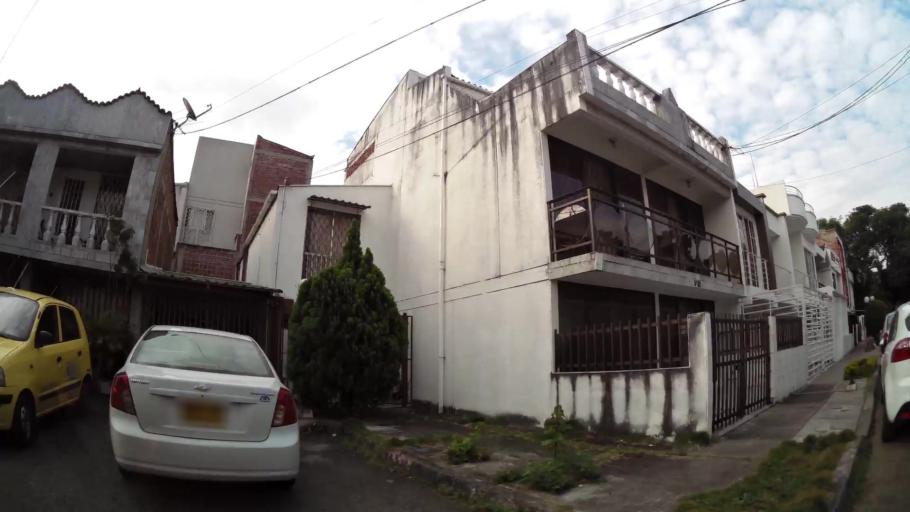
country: CO
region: Valle del Cauca
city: Cali
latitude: 3.4734
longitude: -76.4955
